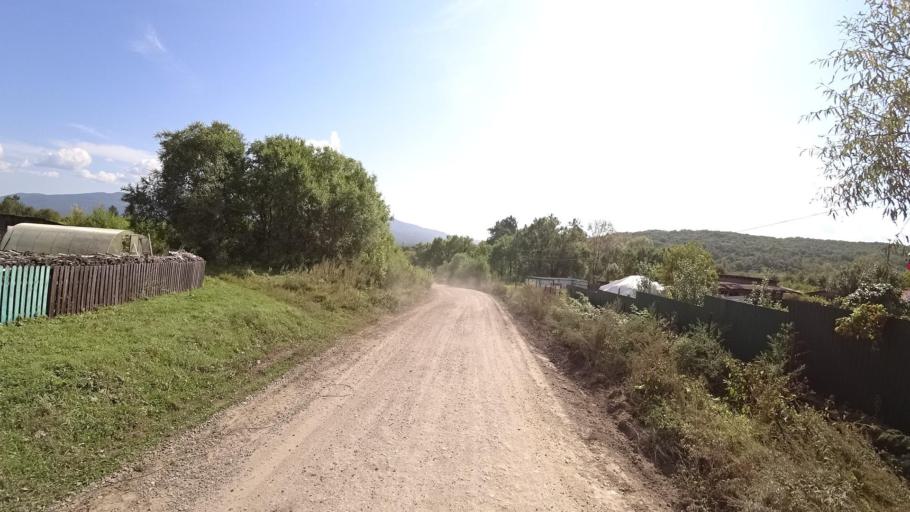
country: RU
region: Jewish Autonomous Oblast
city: Birakan
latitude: 49.0106
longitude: 131.7374
